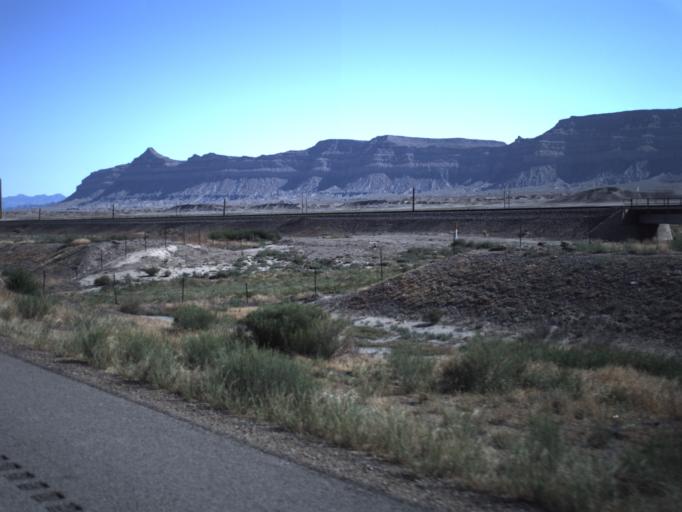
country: US
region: Utah
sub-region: Carbon County
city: East Carbon City
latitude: 39.0967
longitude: -110.3224
